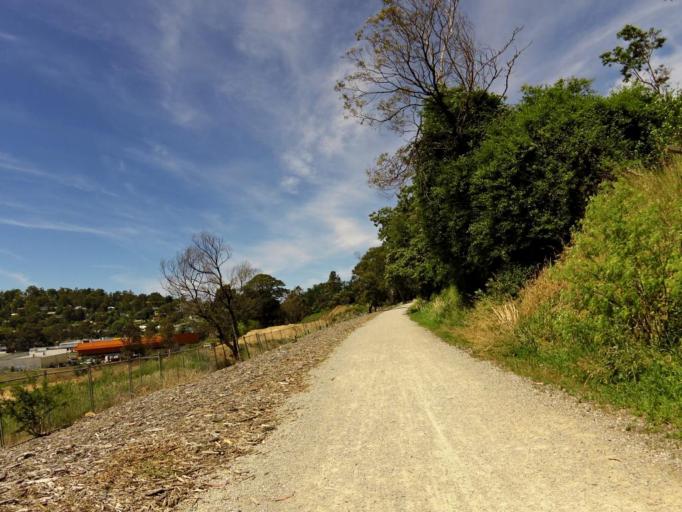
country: AU
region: Victoria
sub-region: Yarra Ranges
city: Lilydale
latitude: -37.7521
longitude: 145.3599
